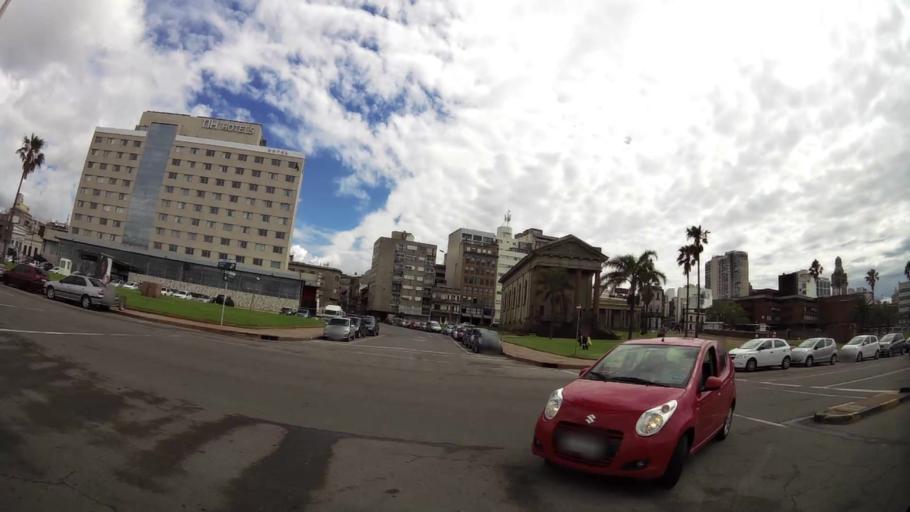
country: UY
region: Montevideo
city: Montevideo
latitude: -34.9104
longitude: -56.2038
